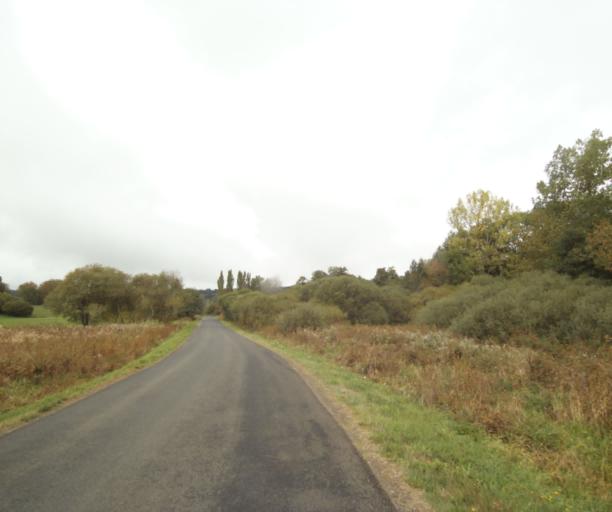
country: FR
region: Auvergne
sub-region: Departement du Puy-de-Dome
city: Saint-Genes-Champanelle
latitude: 45.7215
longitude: 2.9920
